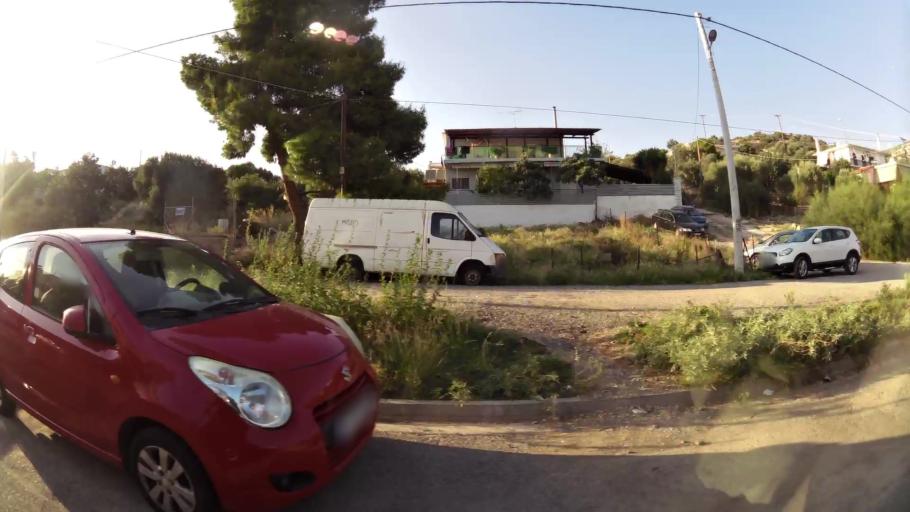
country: GR
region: Attica
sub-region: Nomarchia Athinas
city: Argyroupoli
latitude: 37.8981
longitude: 23.7625
